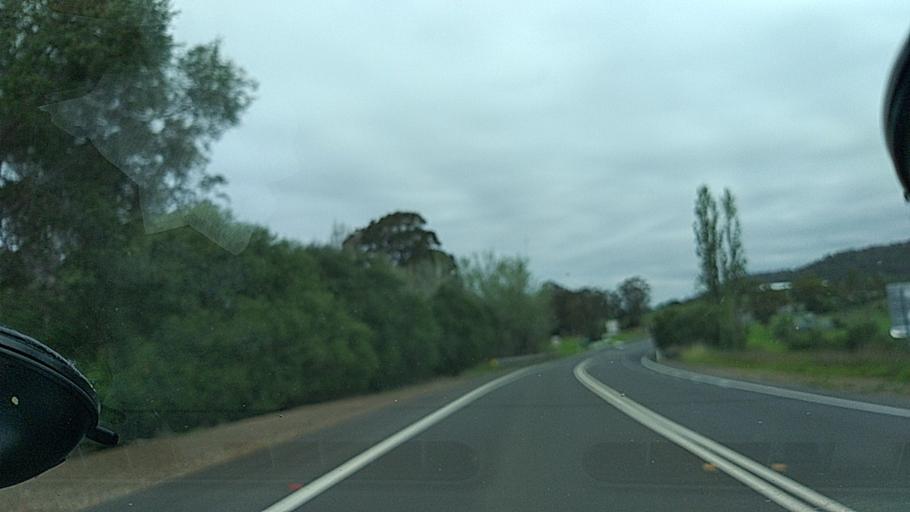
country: AU
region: New South Wales
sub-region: Camden
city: Camden South
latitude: -34.1194
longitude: 150.6990
